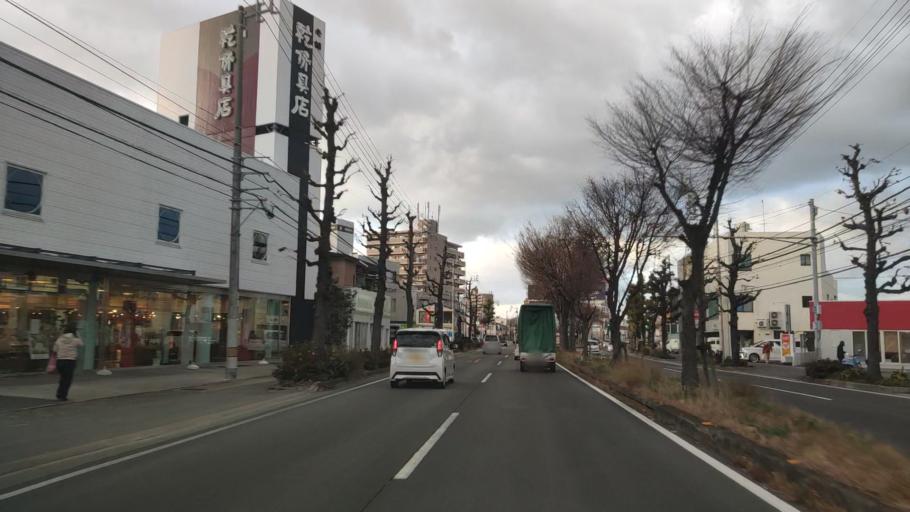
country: JP
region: Ehime
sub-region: Shikoku-chuo Shi
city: Matsuyama
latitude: 33.8147
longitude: 132.7776
